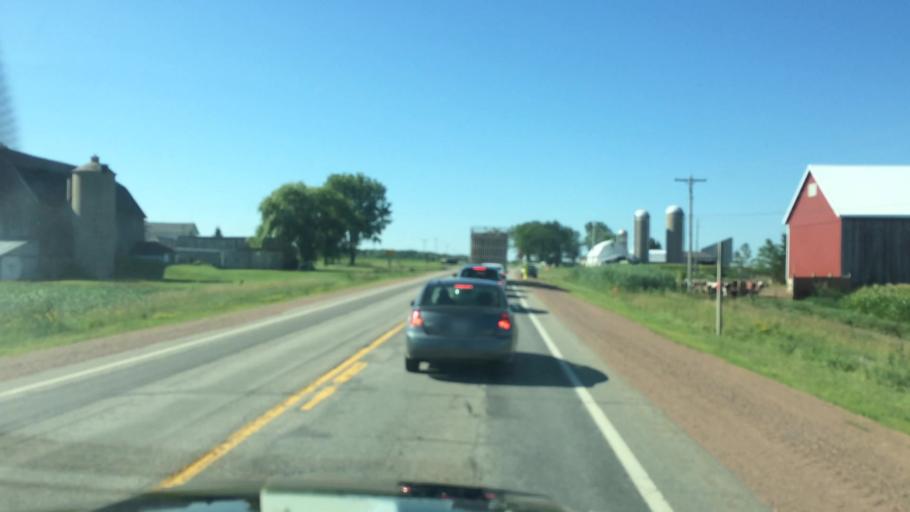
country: US
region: Wisconsin
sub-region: Marathon County
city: Stratford
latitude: 44.9037
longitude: -90.0787
